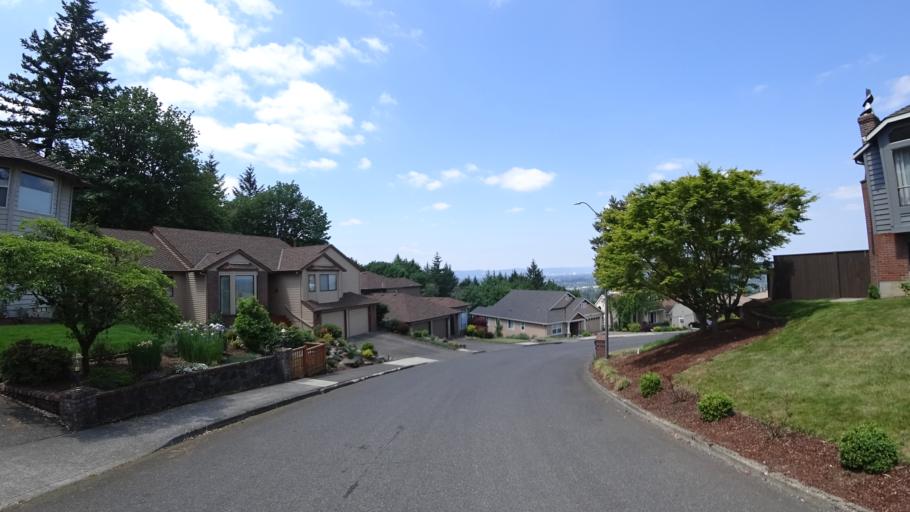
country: US
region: Oregon
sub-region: Clackamas County
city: Happy Valley
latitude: 45.4649
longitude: -122.5196
